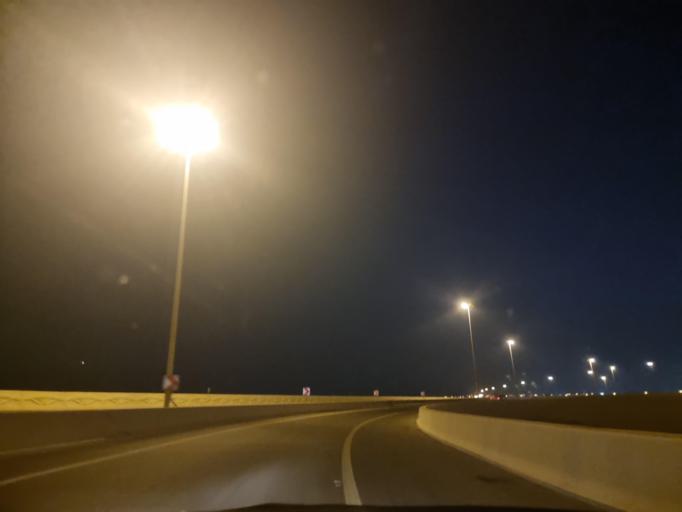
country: AE
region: Abu Dhabi
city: Abu Dhabi
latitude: 24.4174
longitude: 54.7654
